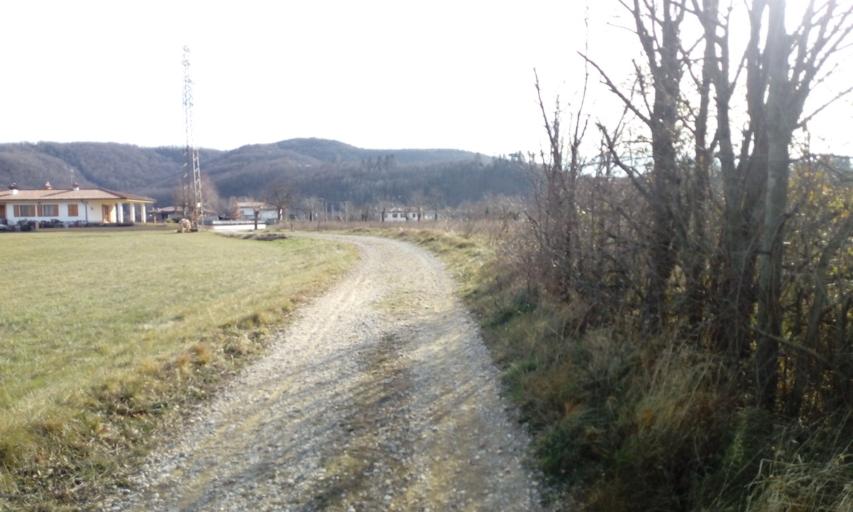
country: IT
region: Friuli Venezia Giulia
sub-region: Provincia di Udine
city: Cividale del Friuli
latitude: 46.0982
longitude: 13.4509
